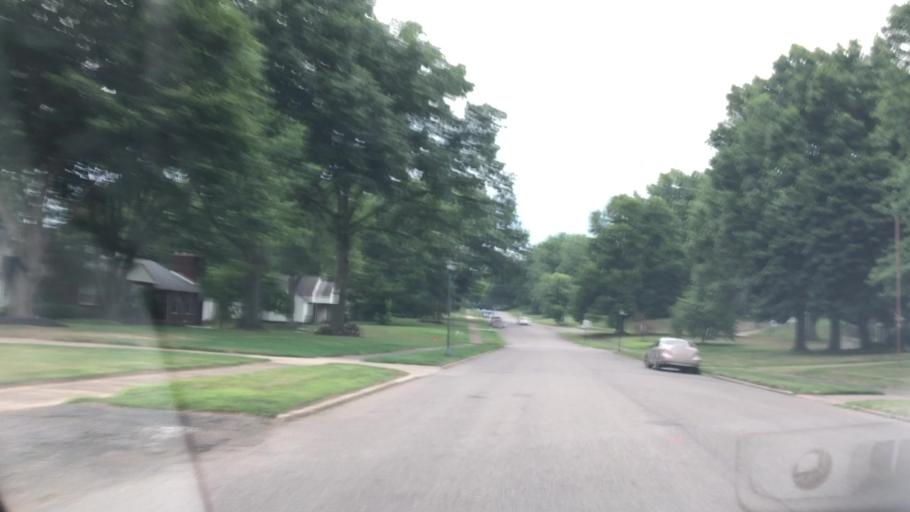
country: US
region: Ohio
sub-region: Stark County
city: Massillon
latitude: 40.8129
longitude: -81.5108
